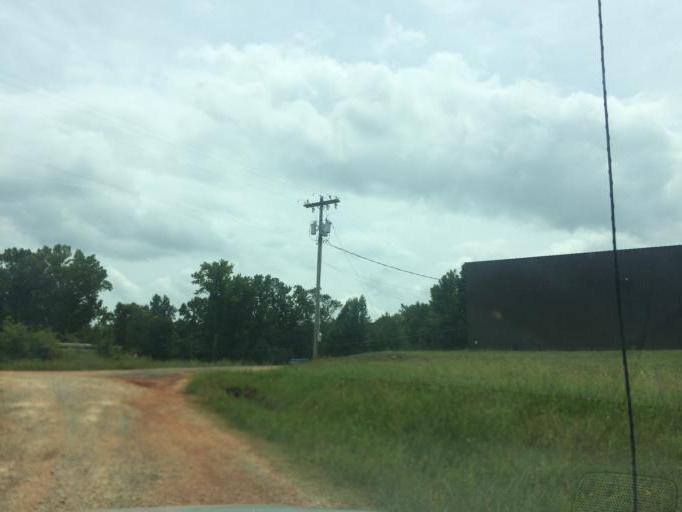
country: US
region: Georgia
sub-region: Elbert County
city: Elberton
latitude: 34.1304
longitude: -82.8629
